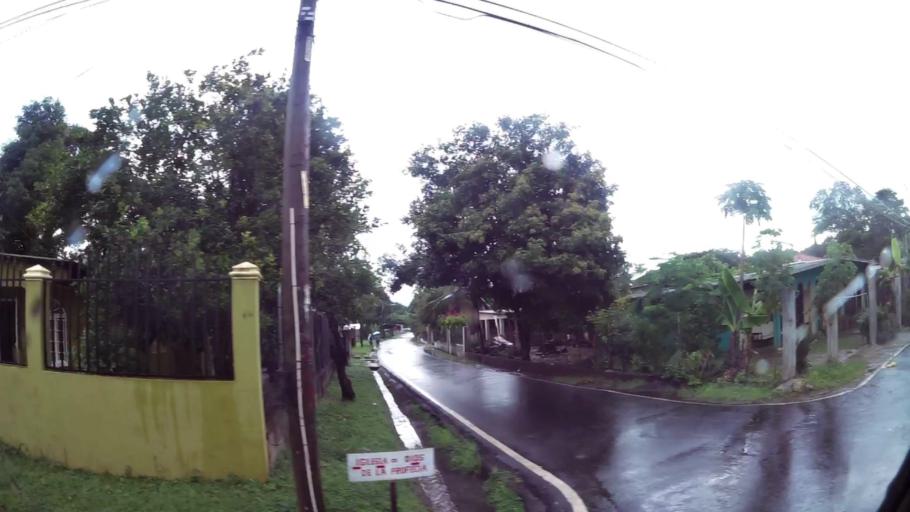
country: PA
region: Panama
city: Cabra Numero Uno
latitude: 9.1005
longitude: -79.3241
